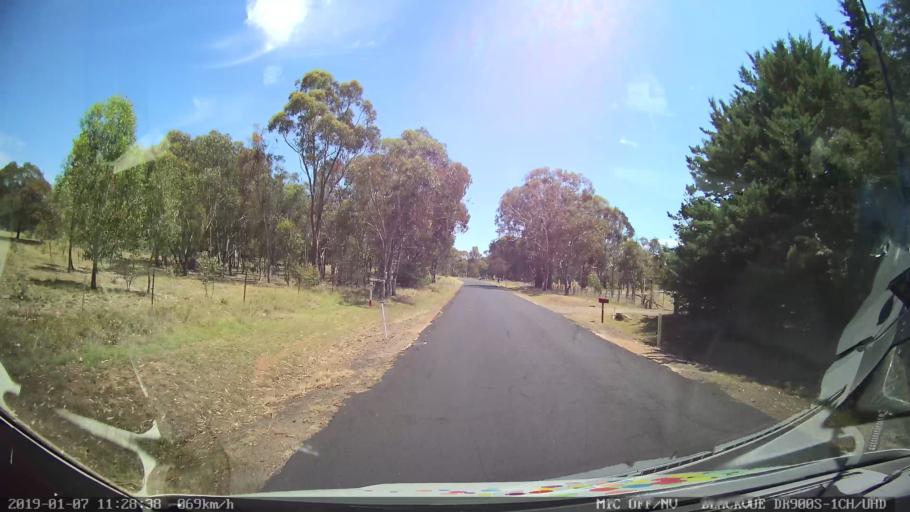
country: AU
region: New South Wales
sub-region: Armidale Dumaresq
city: Armidale
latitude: -30.4467
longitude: 151.5654
